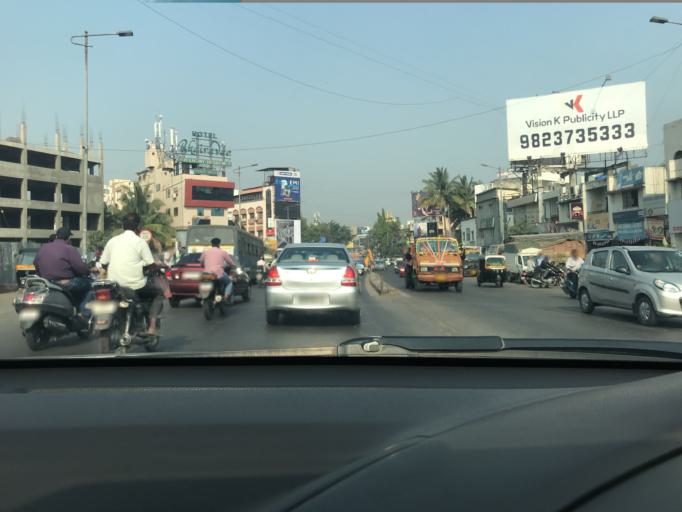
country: IN
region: Maharashtra
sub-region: Pune Division
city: Khadki
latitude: 18.5517
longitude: 73.8042
